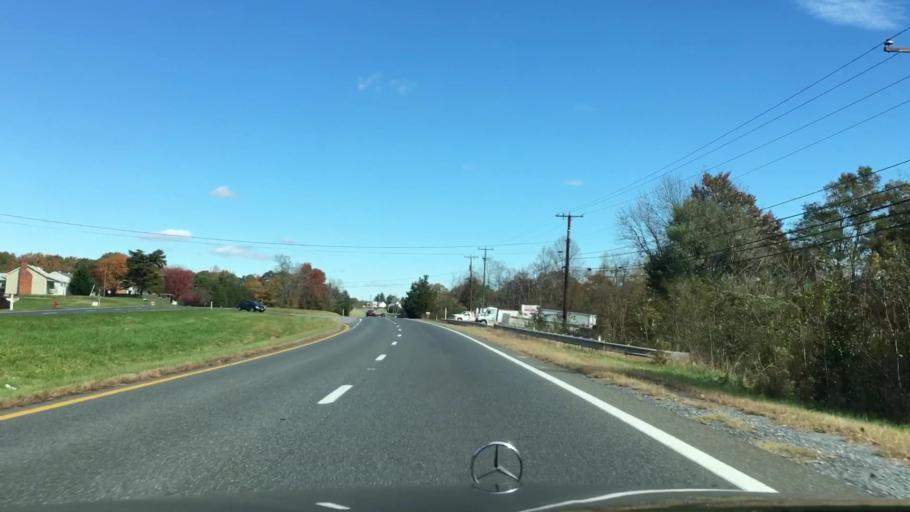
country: US
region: Virginia
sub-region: Campbell County
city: Altavista
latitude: 37.1646
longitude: -79.2151
